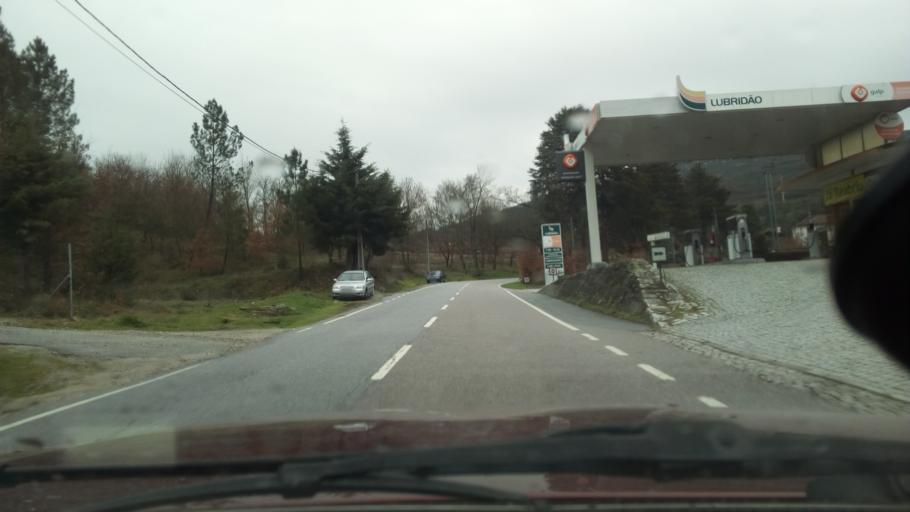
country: PT
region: Viseu
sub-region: Viseu
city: Rio de Loba
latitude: 40.6358
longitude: -7.8257
